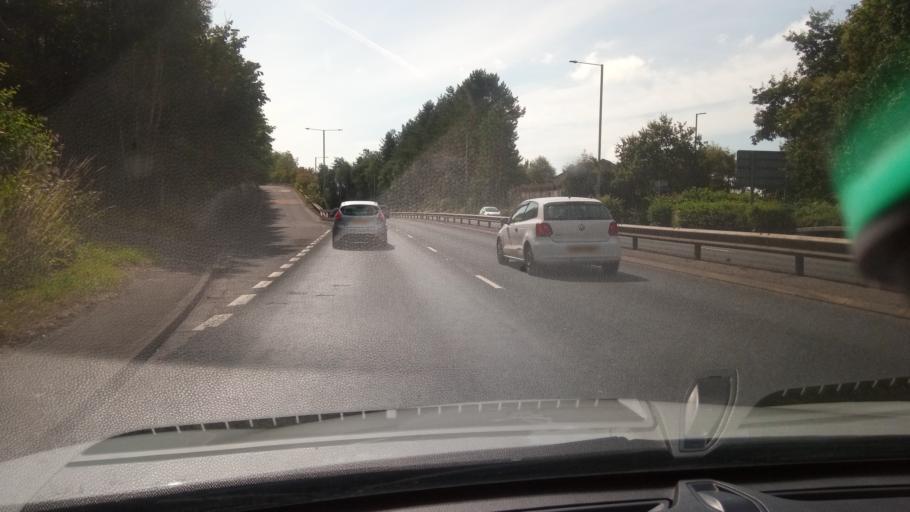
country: GB
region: Wales
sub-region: Rhondda Cynon Taf
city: Llantrisant
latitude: 51.5416
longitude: -3.3856
